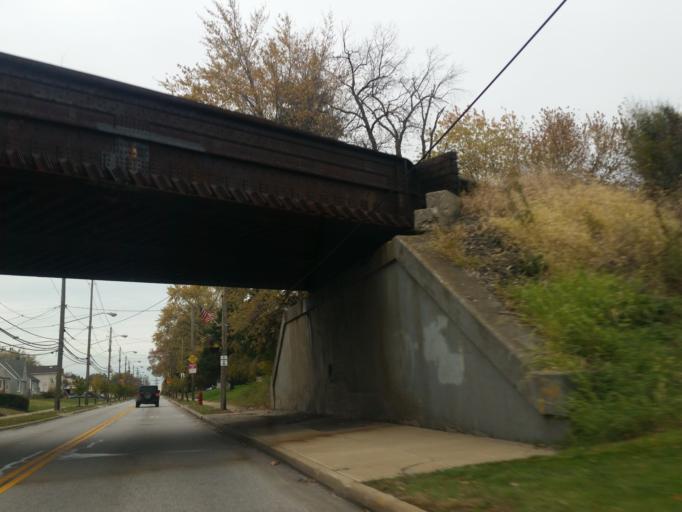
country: US
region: Ohio
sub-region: Cuyahoga County
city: Newburgh Heights
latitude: 41.4310
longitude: -81.6566
